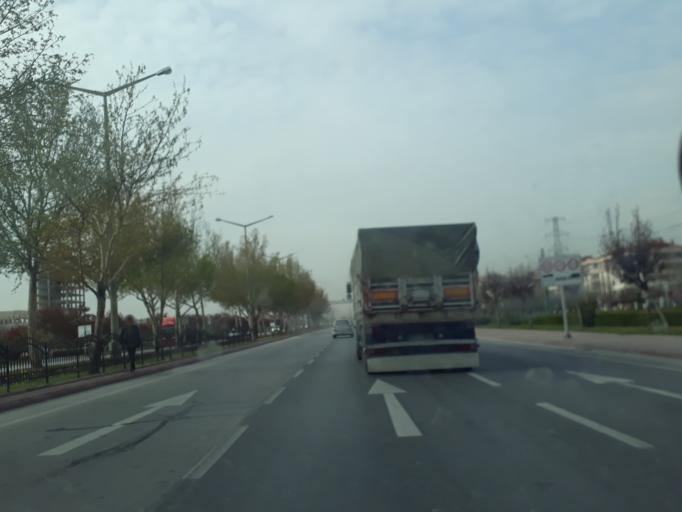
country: TR
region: Konya
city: Selcuklu
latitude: 37.9647
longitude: 32.5148
